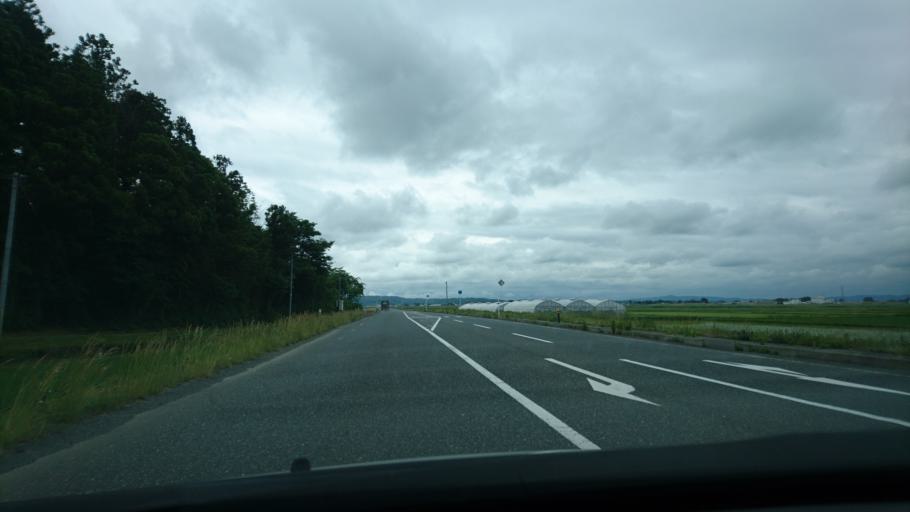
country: JP
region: Miyagi
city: Wakuya
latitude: 38.6956
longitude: 141.2604
